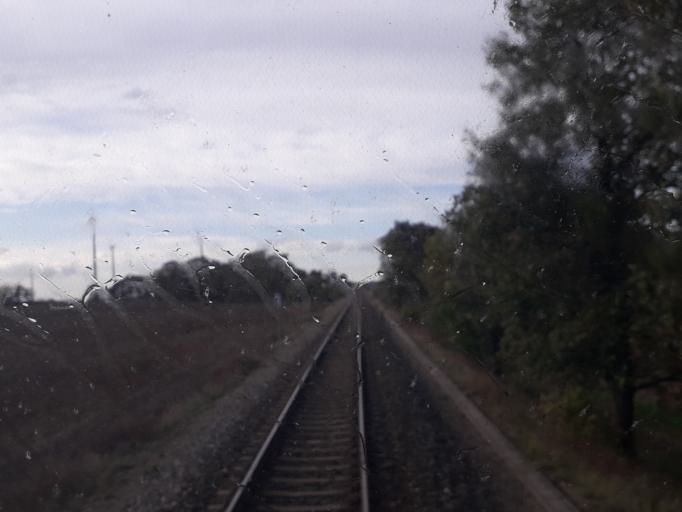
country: DE
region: Brandenburg
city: Wittstock
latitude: 53.1576
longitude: 12.4429
